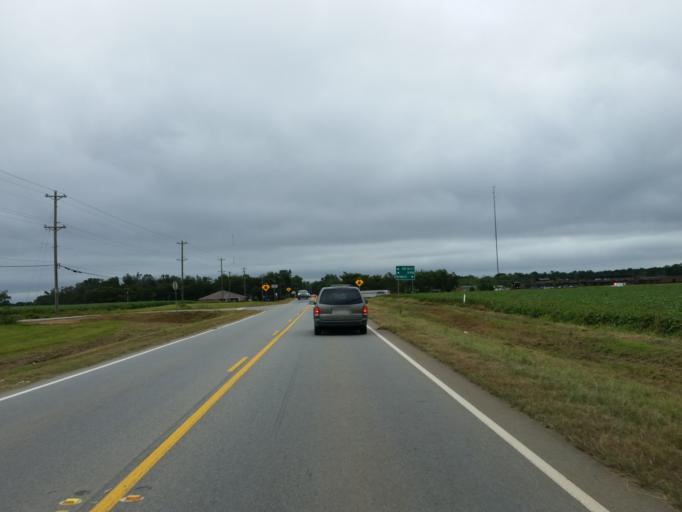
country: US
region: Georgia
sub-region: Peach County
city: Fort Valley
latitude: 32.5782
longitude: -83.9116
